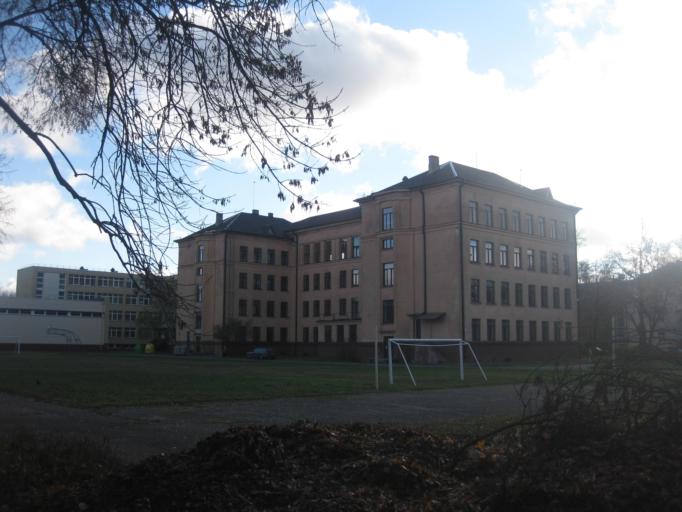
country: LT
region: Kauno apskritis
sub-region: Kaunas
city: Silainiai
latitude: 54.9141
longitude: 23.8916
